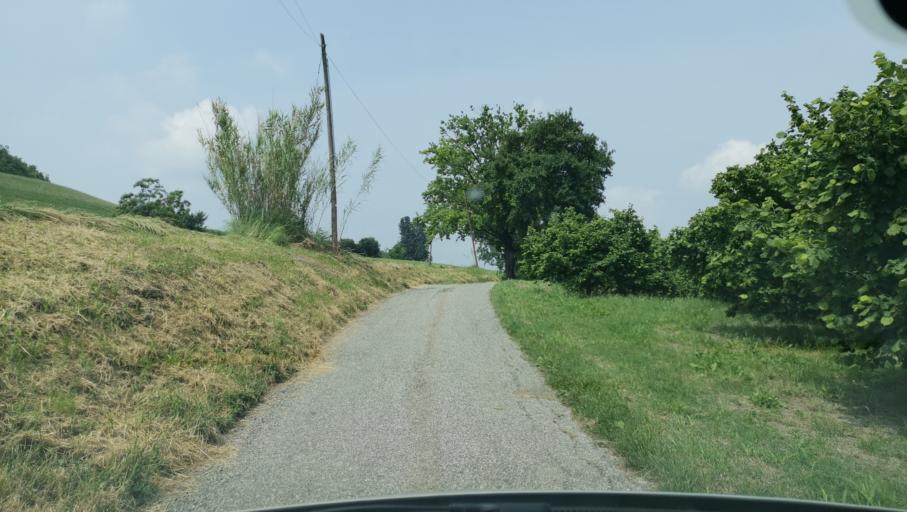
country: IT
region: Piedmont
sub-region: Provincia di Asti
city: Moncalvo
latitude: 45.0591
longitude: 8.2488
